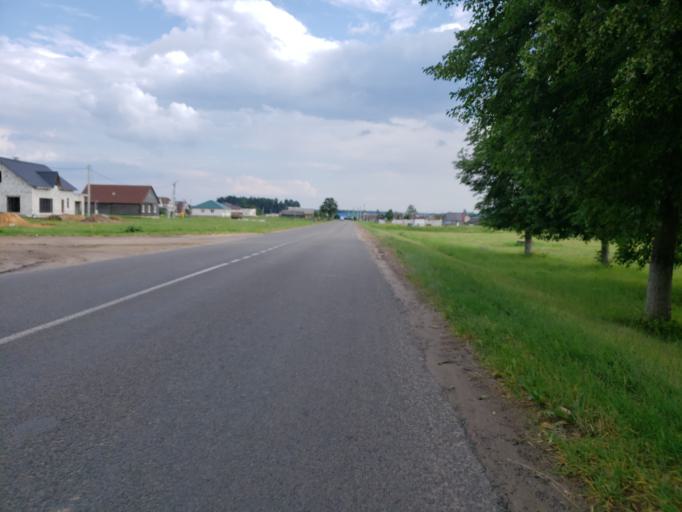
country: BY
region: Minsk
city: Chervyen'
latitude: 53.7336
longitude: 28.3882
